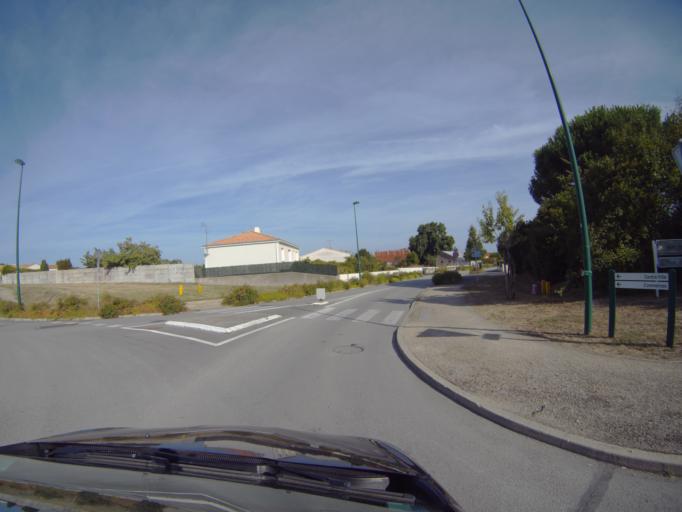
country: FR
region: Pays de la Loire
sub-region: Departement de la Vendee
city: Les Clouzeaux
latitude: 46.6249
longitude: -1.5073
